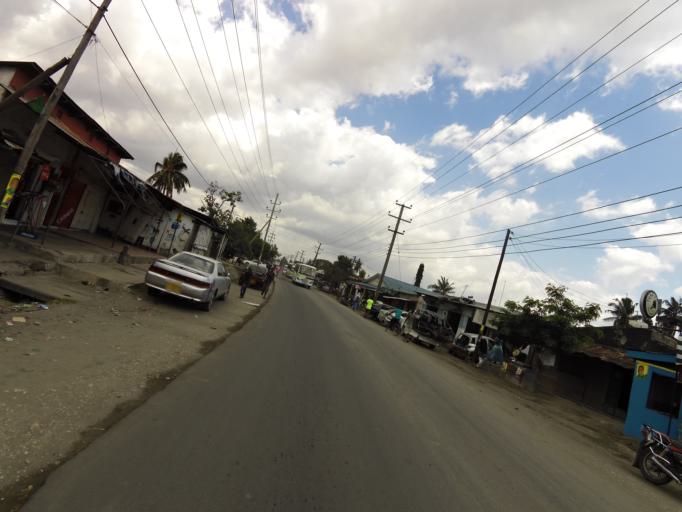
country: TZ
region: Dar es Salaam
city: Magomeni
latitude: -6.7911
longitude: 39.2382
